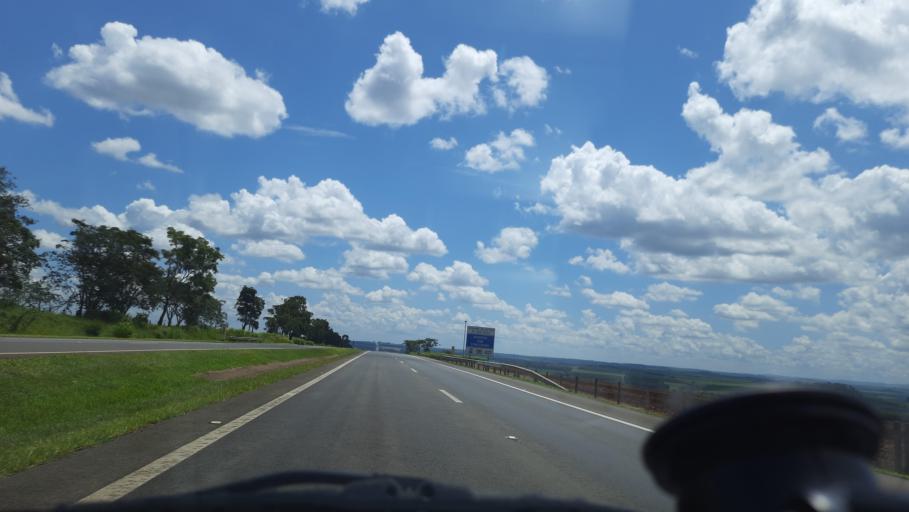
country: BR
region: Sao Paulo
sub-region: Aguai
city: Aguai
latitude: -22.0261
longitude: -47.0336
